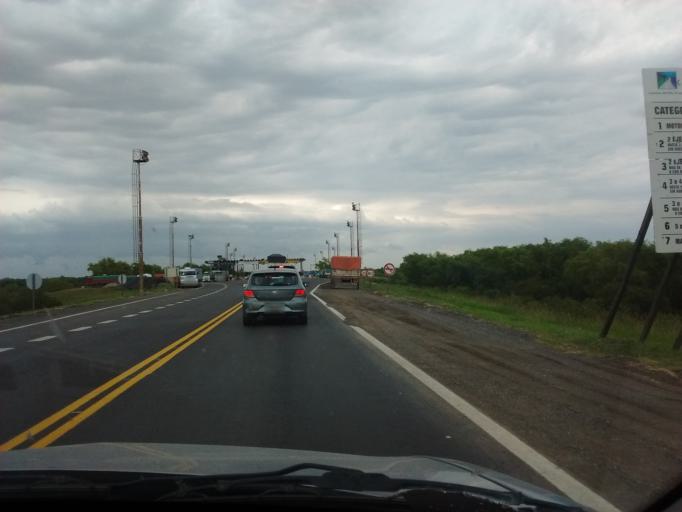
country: AR
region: Santa Fe
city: Granadero Baigorria
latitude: -32.8650
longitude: -60.6481
